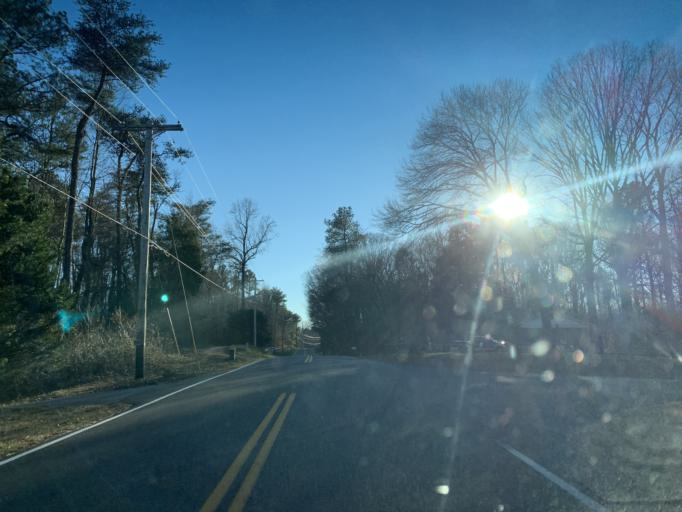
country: US
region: Maryland
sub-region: Saint Mary's County
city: Mechanicsville
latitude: 38.4539
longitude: -76.7123
